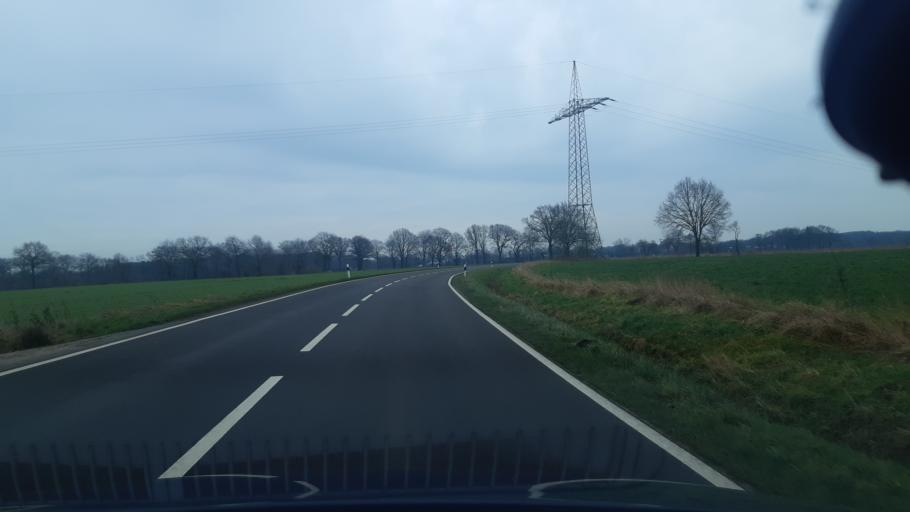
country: DE
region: Lower Saxony
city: Cloppenburg
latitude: 52.8174
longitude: 8.0106
